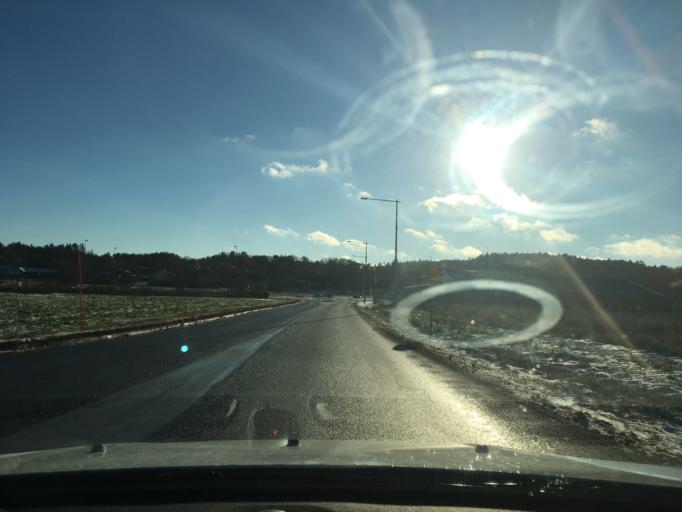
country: SE
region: Vaestra Goetaland
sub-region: Tjorns Kommun
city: Myggenas
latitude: 58.0259
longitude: 11.6565
